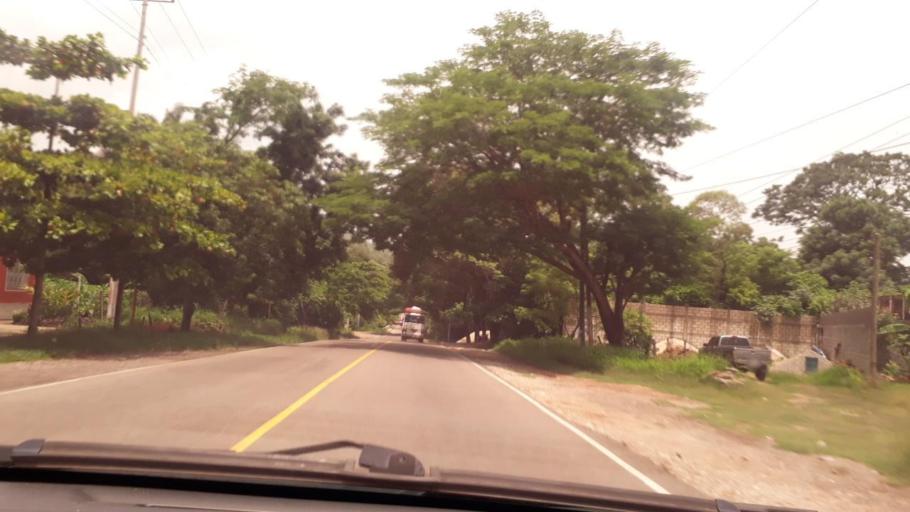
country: GT
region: Chiquimula
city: Quezaltepeque
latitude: 14.6239
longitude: -89.4454
